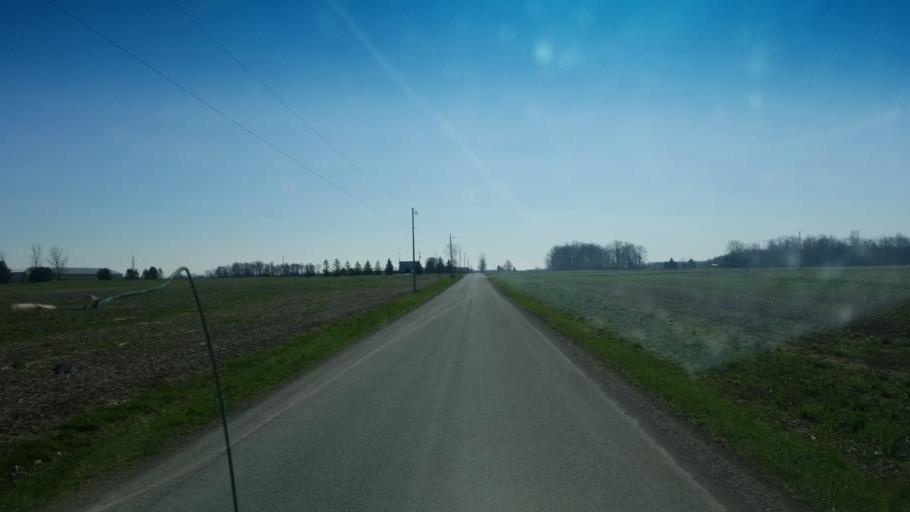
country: US
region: Ohio
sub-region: Hardin County
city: Kenton
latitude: 40.7020
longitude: -83.5329
